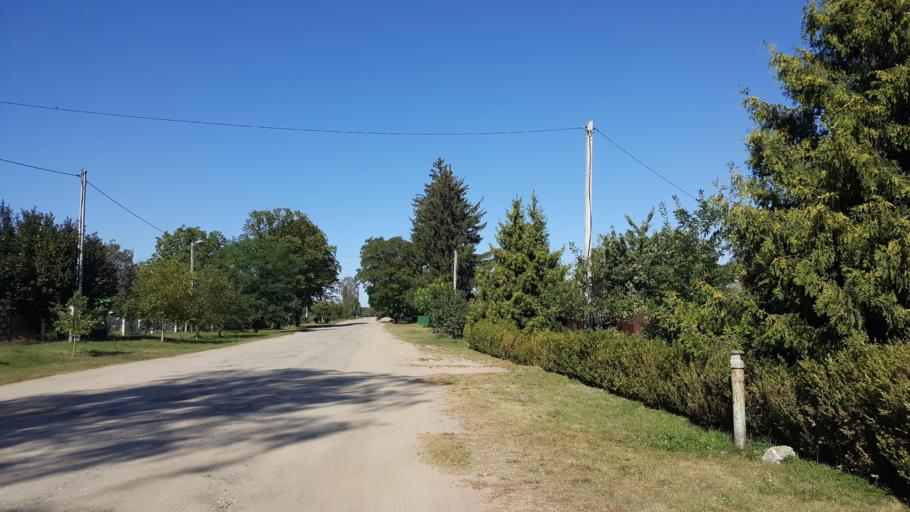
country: BY
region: Brest
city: Vysokaye
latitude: 52.2564
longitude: 23.5029
